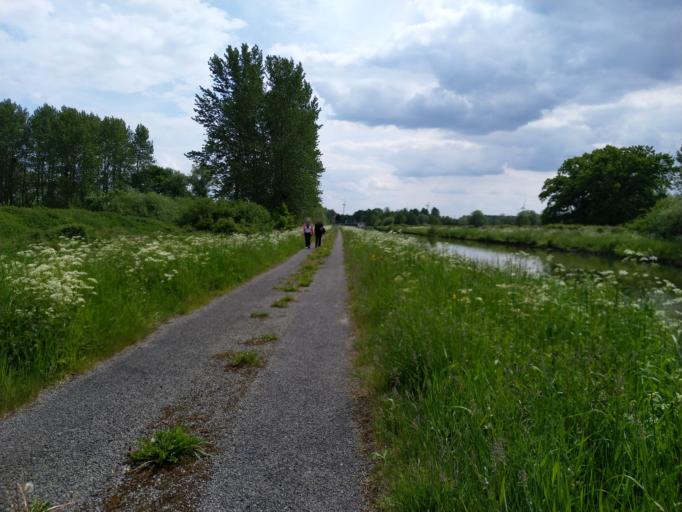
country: FR
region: Picardie
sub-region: Departement de l'Aisne
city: Wassigny
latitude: 50.0518
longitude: 3.6432
